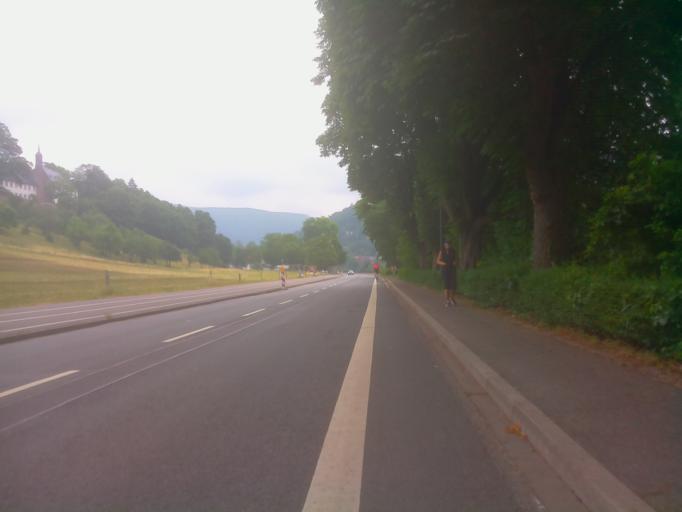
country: DE
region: Baden-Wuerttemberg
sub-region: Karlsruhe Region
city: Heidelberg
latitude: 49.4188
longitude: 8.7368
